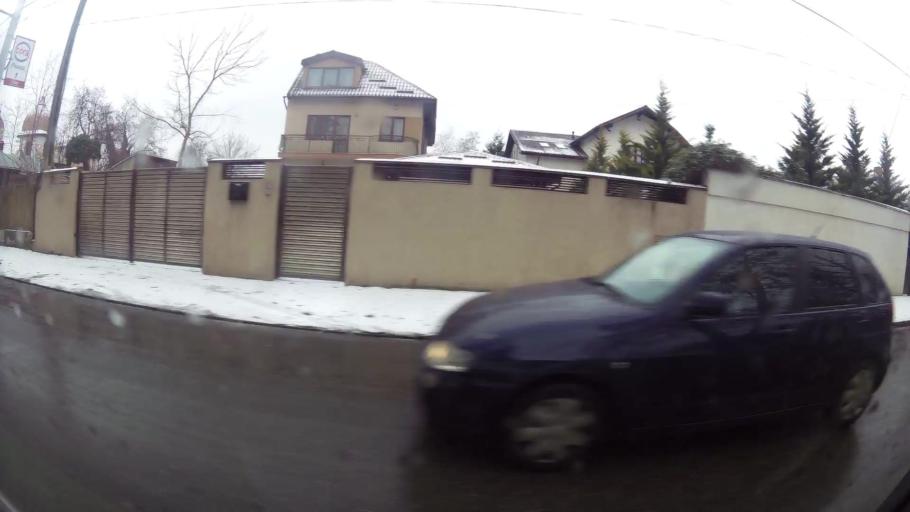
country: RO
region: Prahova
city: Ploiesti
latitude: 44.9403
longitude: 26.0079
